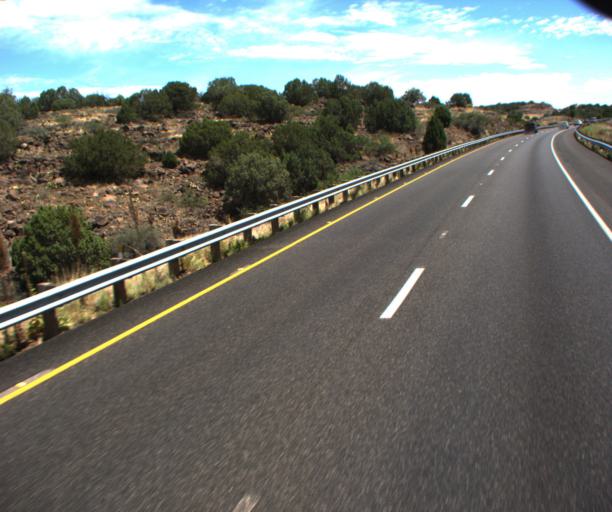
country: US
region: Arizona
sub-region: Yavapai County
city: Big Park
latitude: 34.7191
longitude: -111.7209
